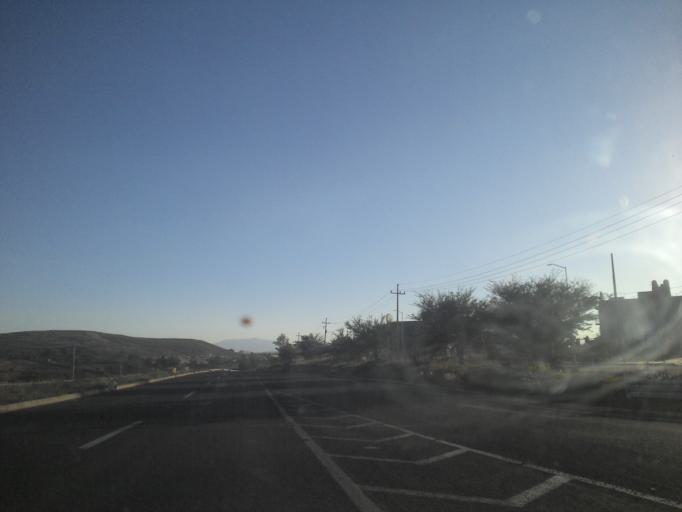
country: MX
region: Jalisco
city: Zapotlanejo
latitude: 20.6210
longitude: -103.0549
